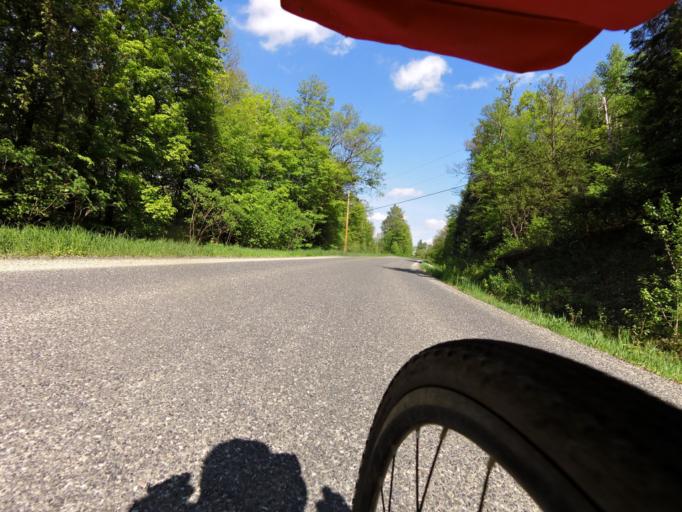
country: CA
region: Ontario
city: Renfrew
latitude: 45.1458
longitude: -76.5677
